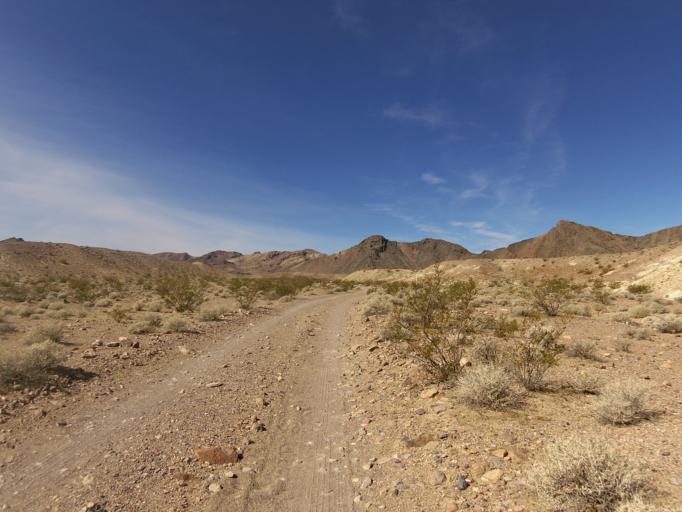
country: US
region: Nevada
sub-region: Nye County
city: Pahrump
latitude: 35.9734
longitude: -116.2756
